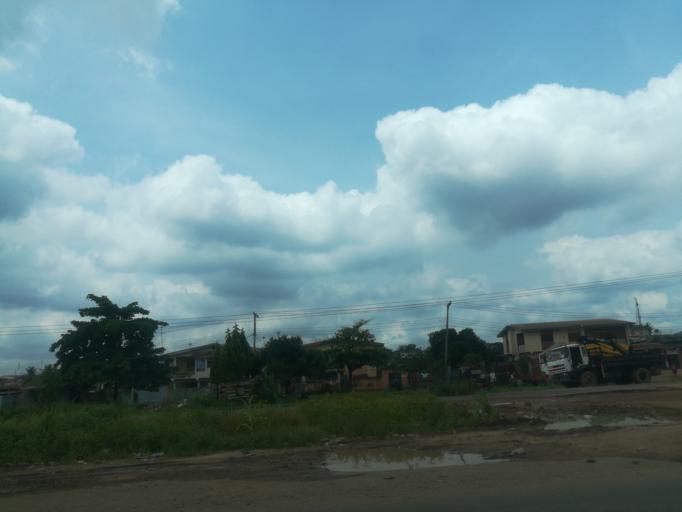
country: NG
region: Oyo
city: Ibadan
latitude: 7.4147
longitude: 3.9428
